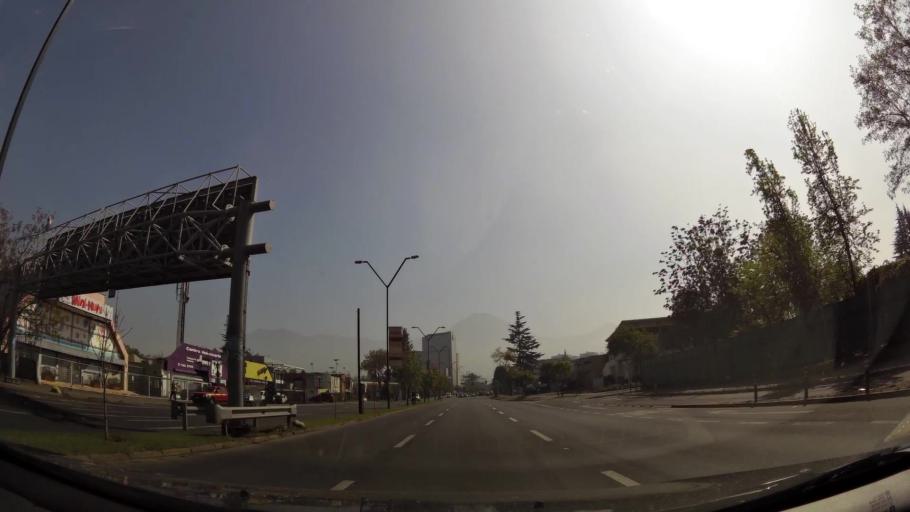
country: CL
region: Santiago Metropolitan
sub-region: Provincia de Santiago
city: Villa Presidente Frei, Nunoa, Santiago, Chile
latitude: -33.3964
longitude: -70.5716
